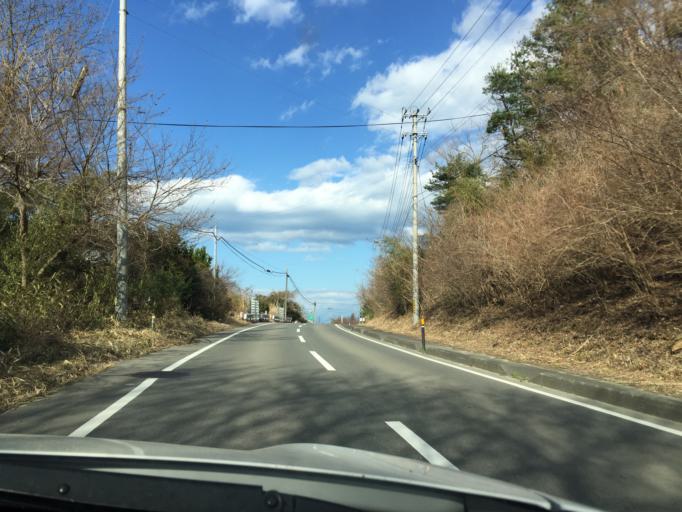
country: JP
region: Fukushima
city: Namie
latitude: 37.4138
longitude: 140.9944
